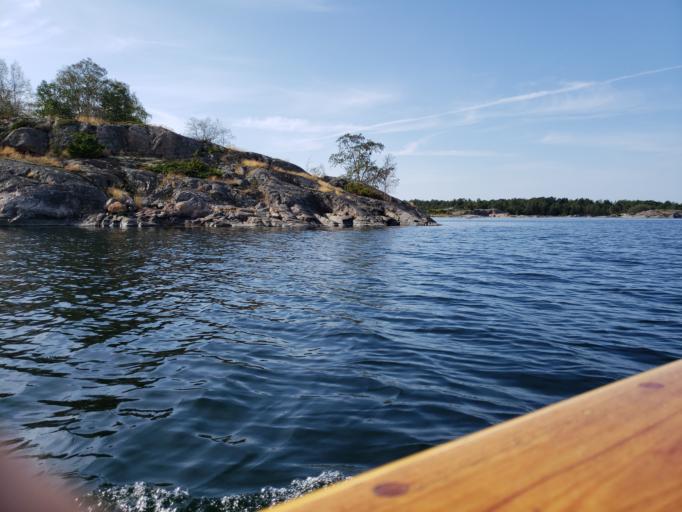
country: FI
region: Varsinais-Suomi
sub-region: Aboland-Turunmaa
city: Dragsfjaerd
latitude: 59.8528
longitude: 22.2130
